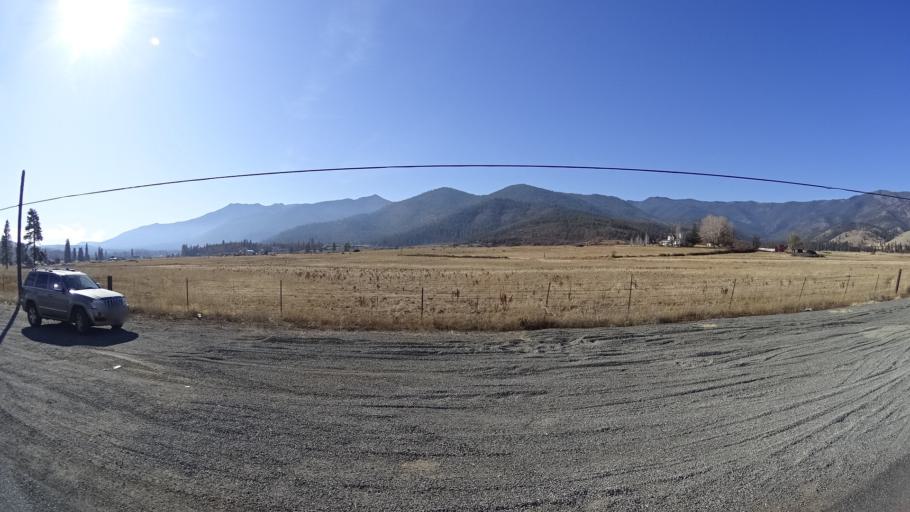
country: US
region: California
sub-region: Siskiyou County
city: Weed
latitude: 41.4416
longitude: -122.4376
